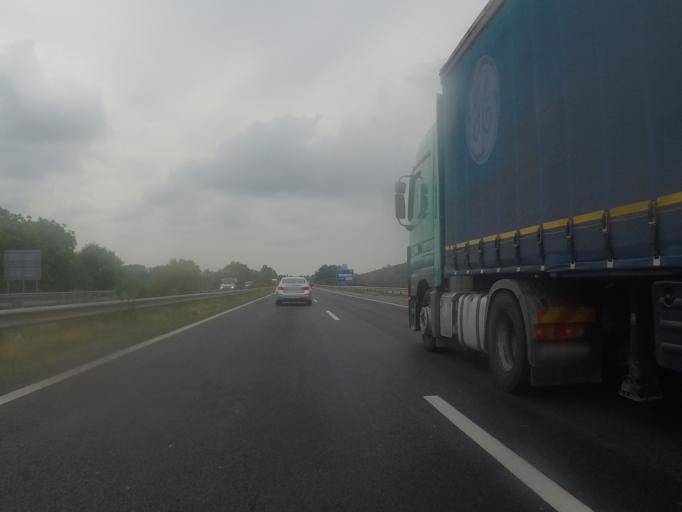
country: HU
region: Somogy
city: Balatonszabadi
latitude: 46.9466
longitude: 18.1494
